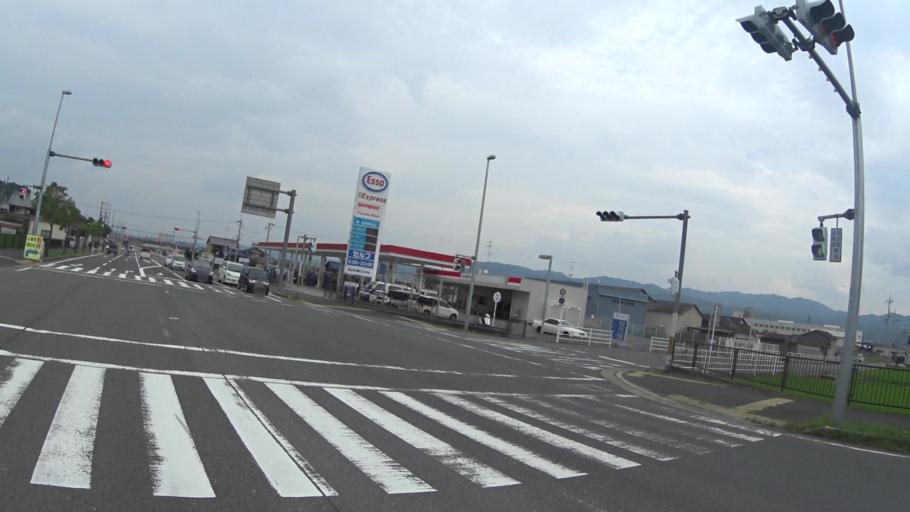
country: JP
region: Kyoto
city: Tanabe
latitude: 34.7677
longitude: 135.7878
